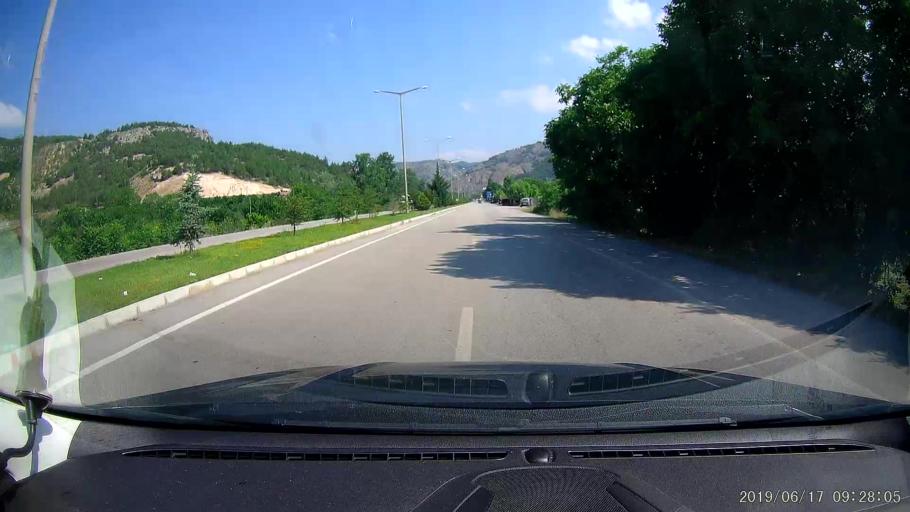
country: TR
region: Amasya
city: Amasya
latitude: 40.6844
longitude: 35.8232
